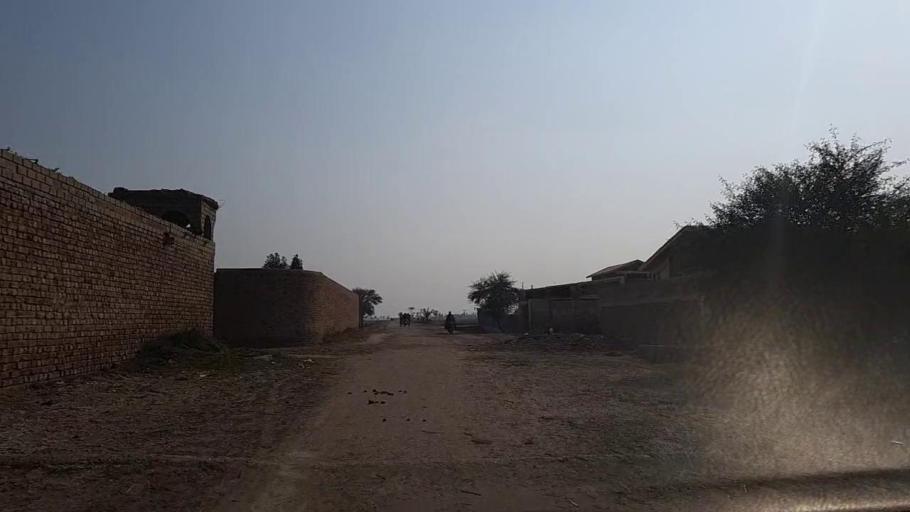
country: PK
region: Sindh
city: Daur
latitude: 26.4138
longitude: 68.4126
